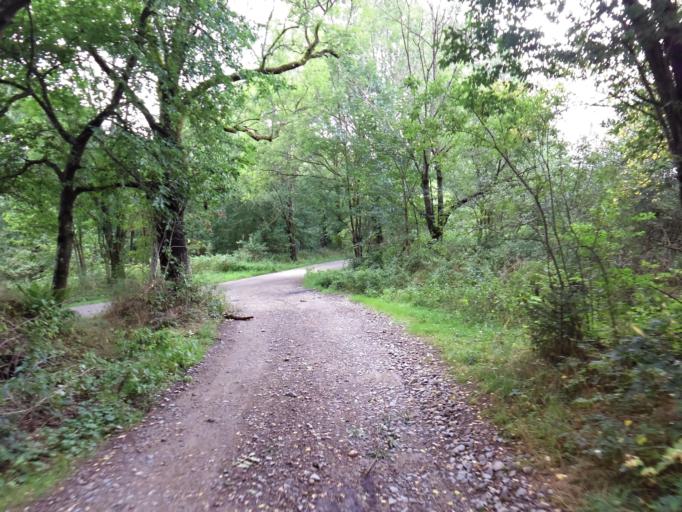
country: CZ
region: Jihocesky
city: Horni Stropnice
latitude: 48.7385
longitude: 14.7615
